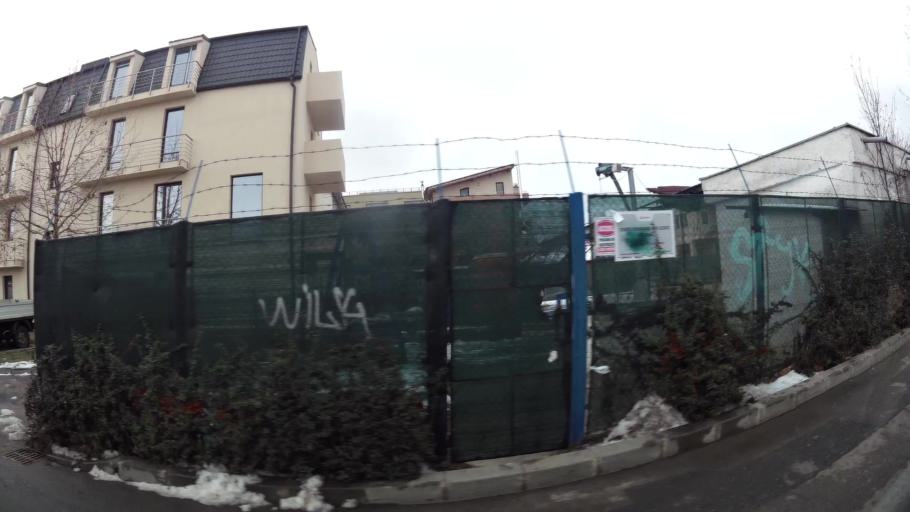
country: RO
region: Ilfov
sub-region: Comuna Otopeni
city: Otopeni
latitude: 44.5461
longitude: 26.0721
